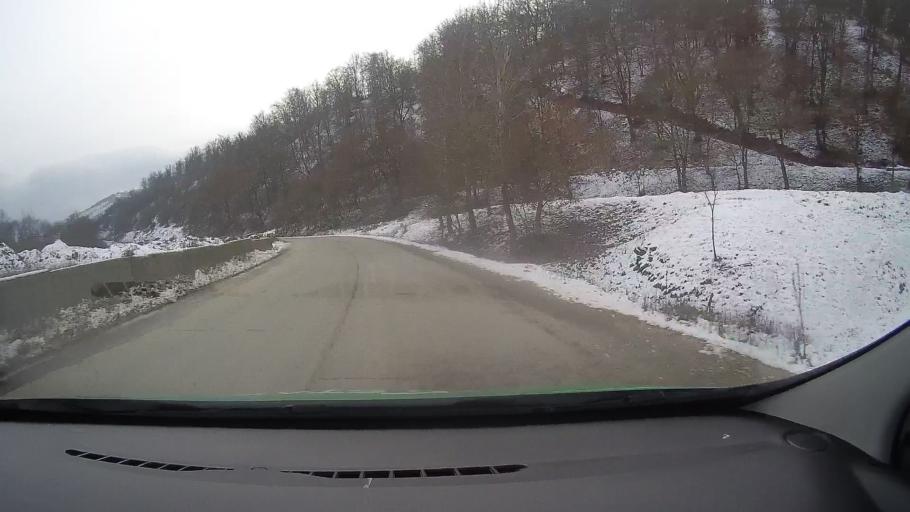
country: RO
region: Alba
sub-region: Oras Zlatna
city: Zlatna
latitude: 46.1181
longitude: 23.2056
